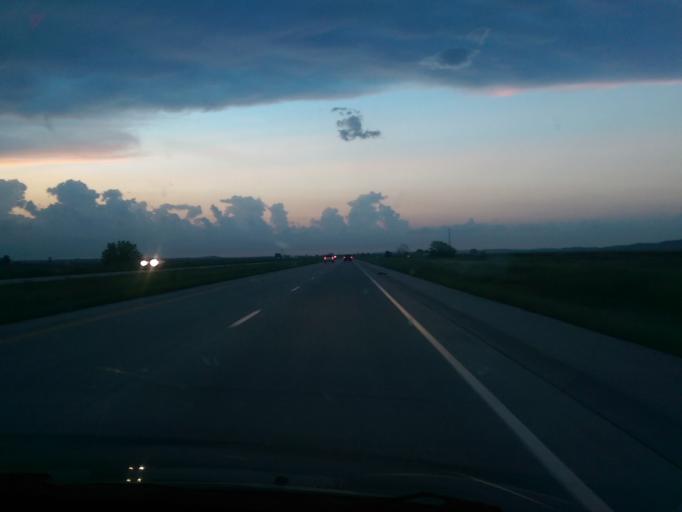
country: US
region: Nebraska
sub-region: Otoe County
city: Nebraska City
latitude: 40.7891
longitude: -95.8070
